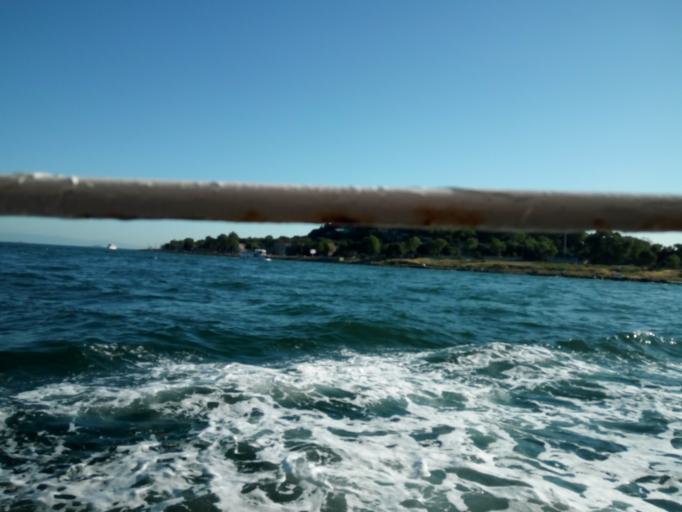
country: TR
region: Istanbul
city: Eminoenue
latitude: 41.0183
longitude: 28.9895
